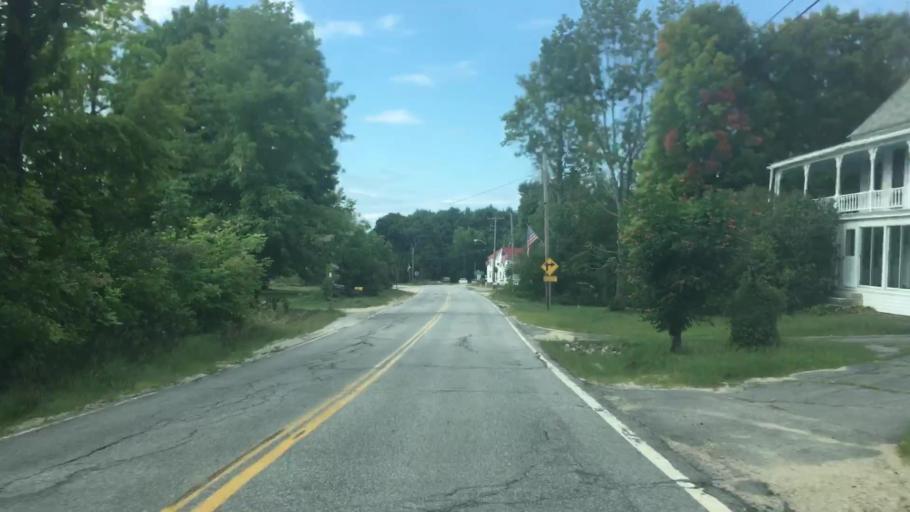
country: US
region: Maine
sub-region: Oxford County
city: Oxford
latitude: 44.0557
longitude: -70.5547
